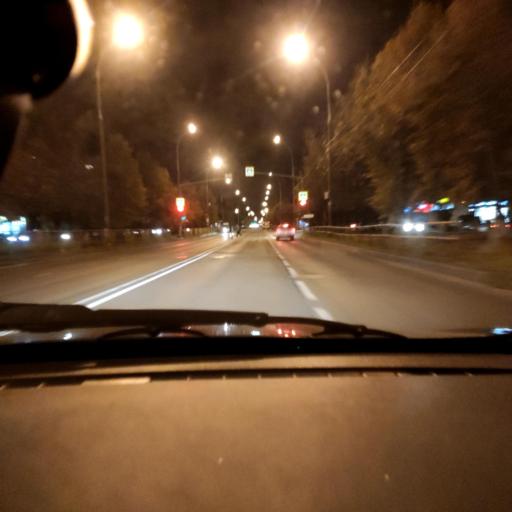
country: RU
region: Samara
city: Tol'yatti
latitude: 53.5302
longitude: 49.3127
